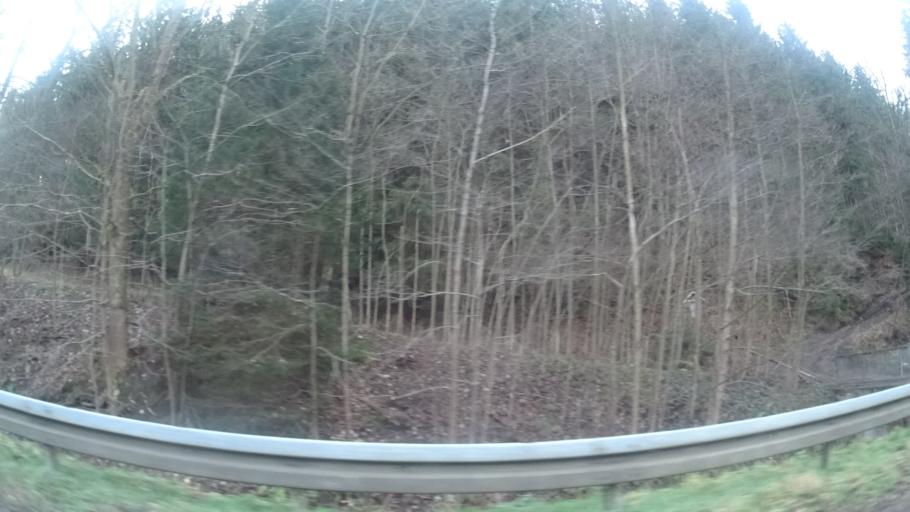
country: DE
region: Thuringia
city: Rohrbach
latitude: 50.6141
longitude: 11.2166
